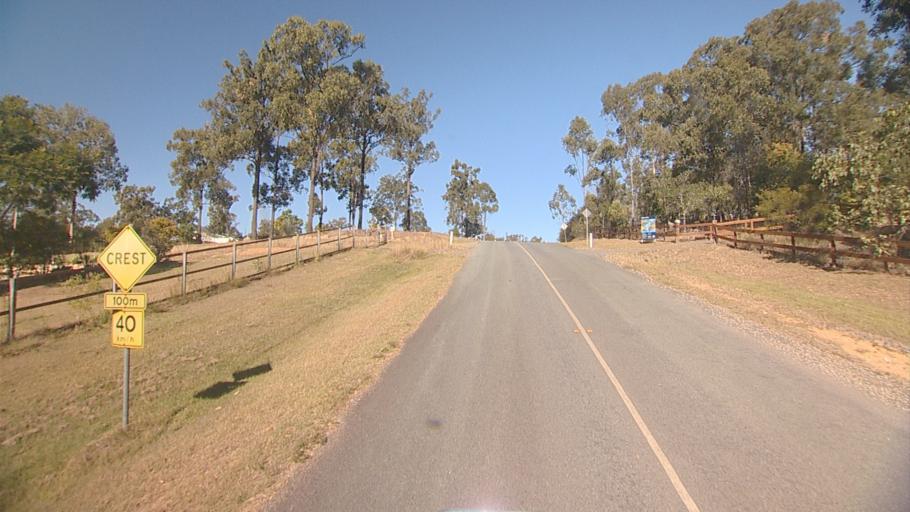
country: AU
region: Queensland
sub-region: Ipswich
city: Springfield Lakes
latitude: -27.7147
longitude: 152.9166
